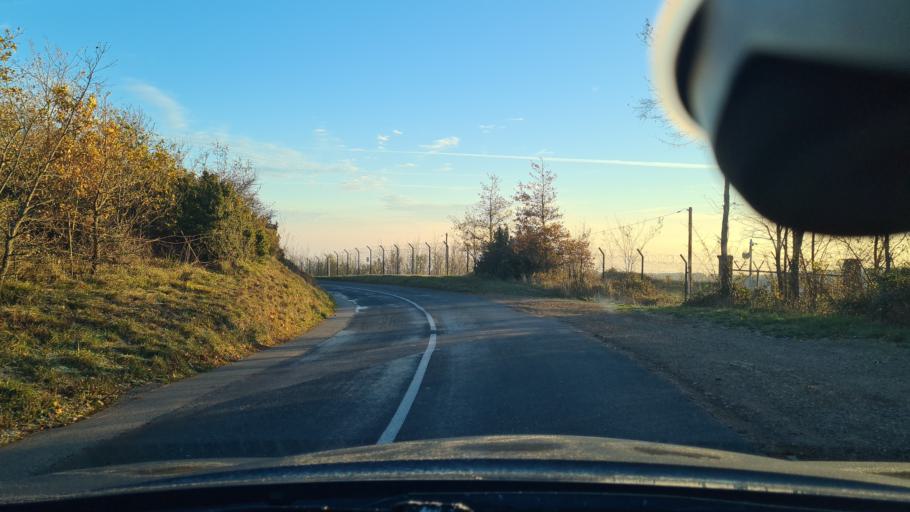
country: FR
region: Rhone-Alpes
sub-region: Departement du Rhone
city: Limonest
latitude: 45.8492
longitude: 4.7824
